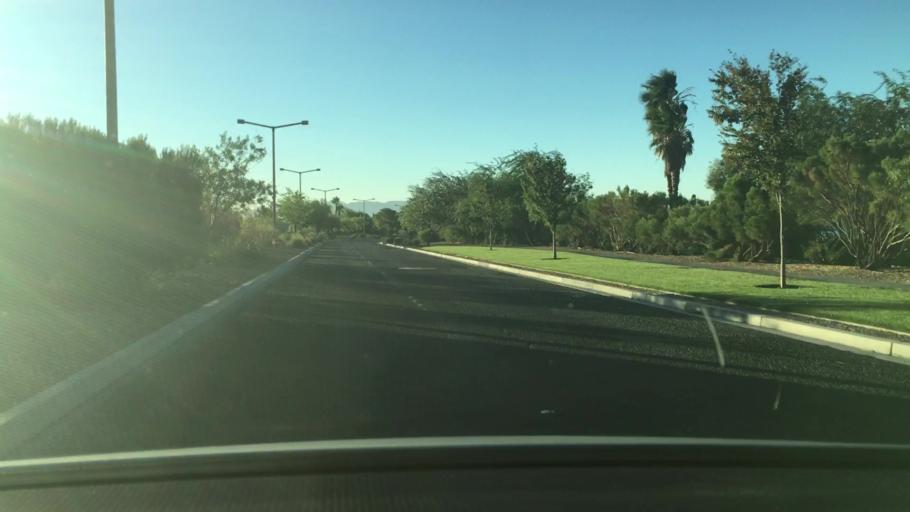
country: US
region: Nevada
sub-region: Clark County
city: Summerlin South
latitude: 36.1252
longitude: -115.3386
